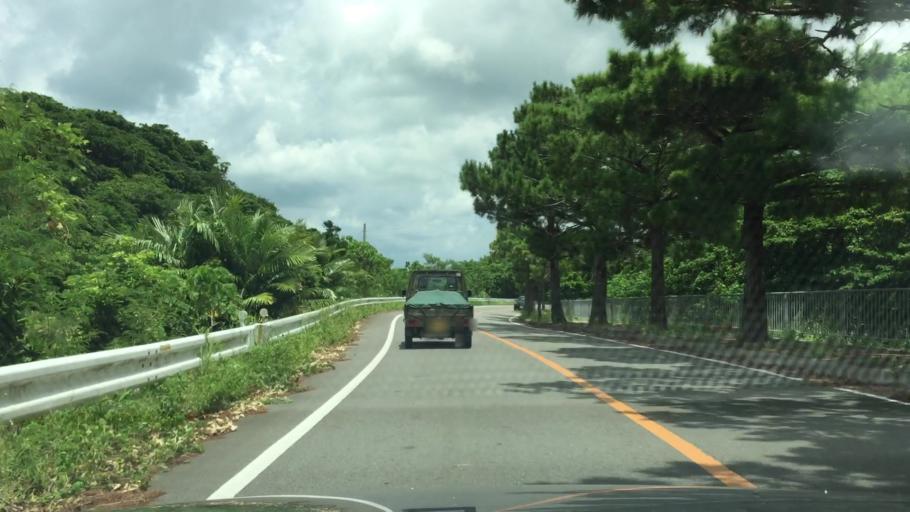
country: JP
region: Okinawa
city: Ishigaki
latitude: 24.3809
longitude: 124.1536
